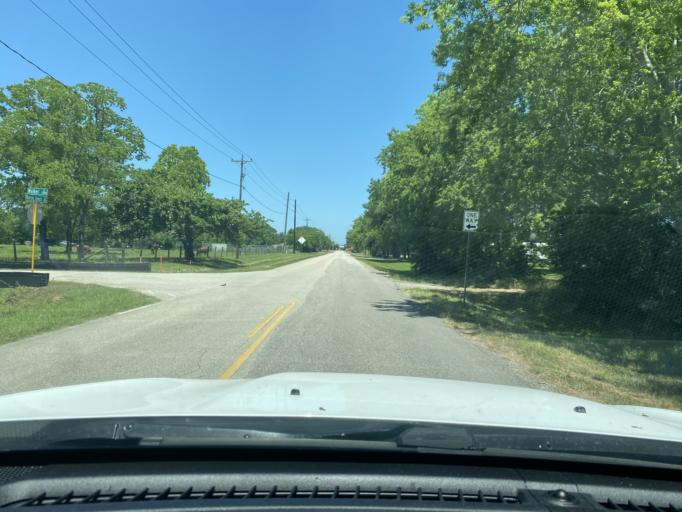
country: US
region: Texas
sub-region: Waller County
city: Waller
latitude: 30.0233
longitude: -95.8475
